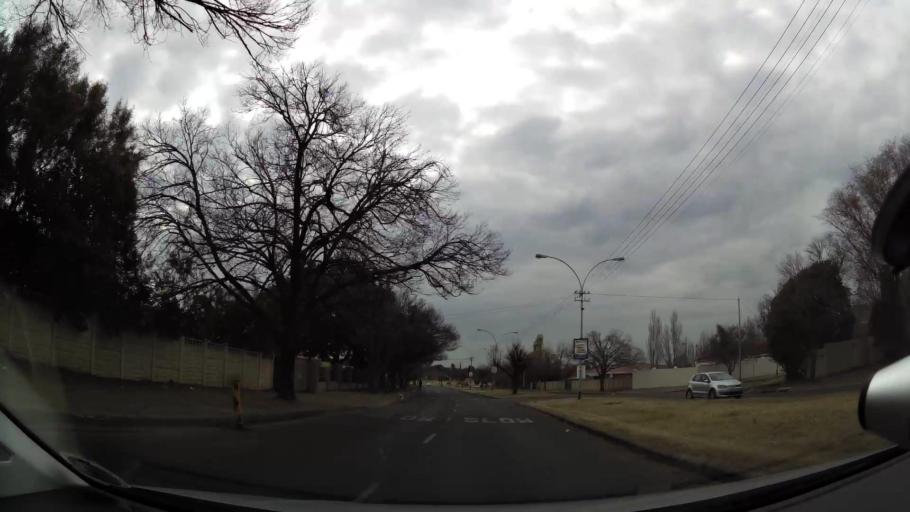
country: ZA
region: Orange Free State
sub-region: Mangaung Metropolitan Municipality
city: Bloemfontein
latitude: -29.0909
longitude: 26.2150
